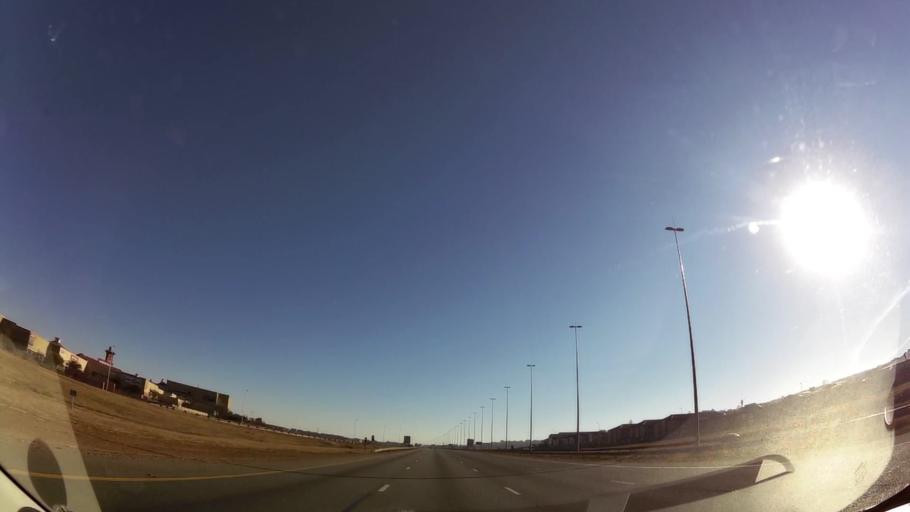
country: ZA
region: Gauteng
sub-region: City of Tshwane Metropolitan Municipality
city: Centurion
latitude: -25.8635
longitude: 28.2534
